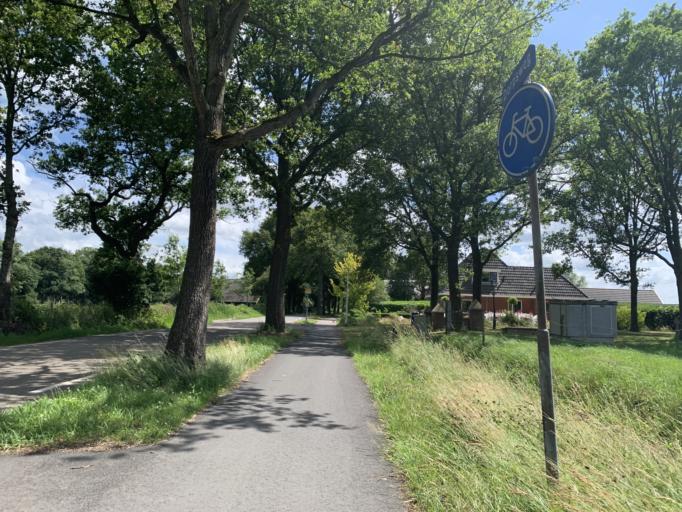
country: NL
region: Groningen
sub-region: Gemeente Haren
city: Haren
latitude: 53.1504
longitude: 6.6464
